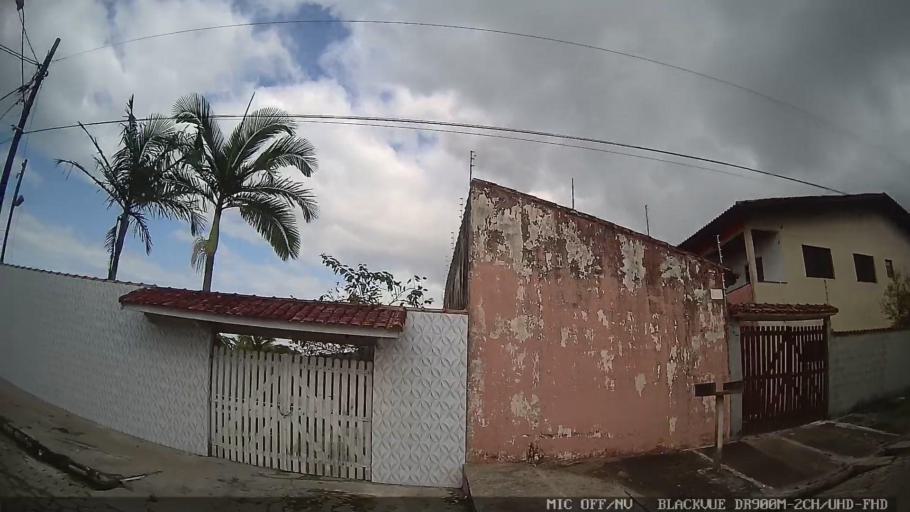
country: BR
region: Sao Paulo
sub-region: Itanhaem
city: Itanhaem
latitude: -24.1993
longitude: -46.8399
